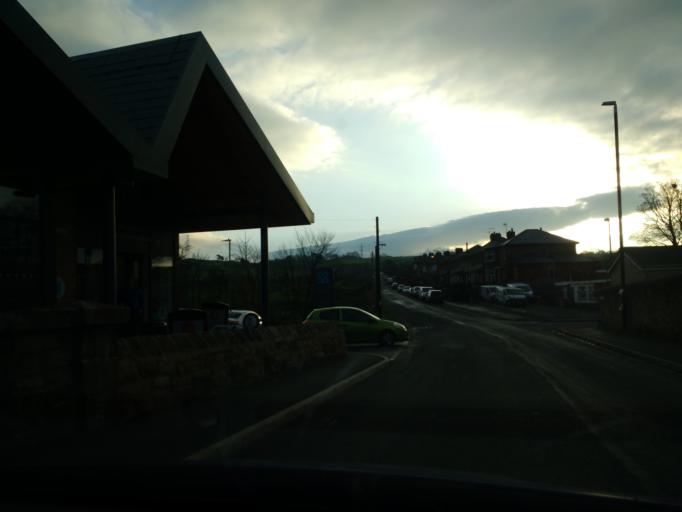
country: GB
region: England
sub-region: Lancashire
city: Lancaster
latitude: 54.0472
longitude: -2.7718
